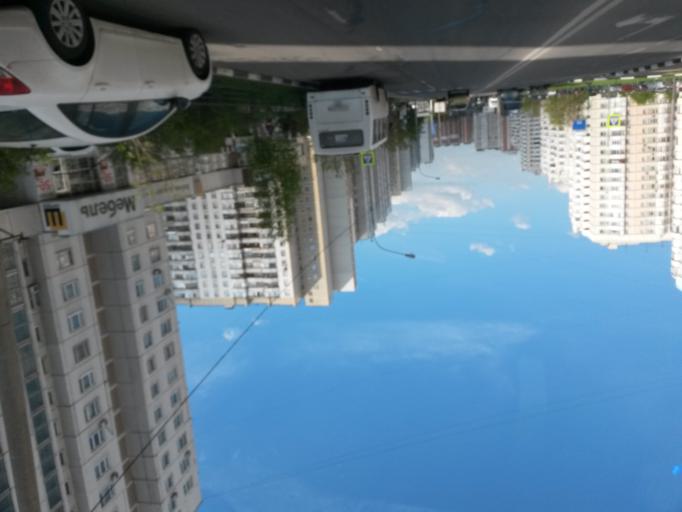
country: RU
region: Moscow
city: Chertanovo Yuzhnoye
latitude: 55.5690
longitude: 37.5637
